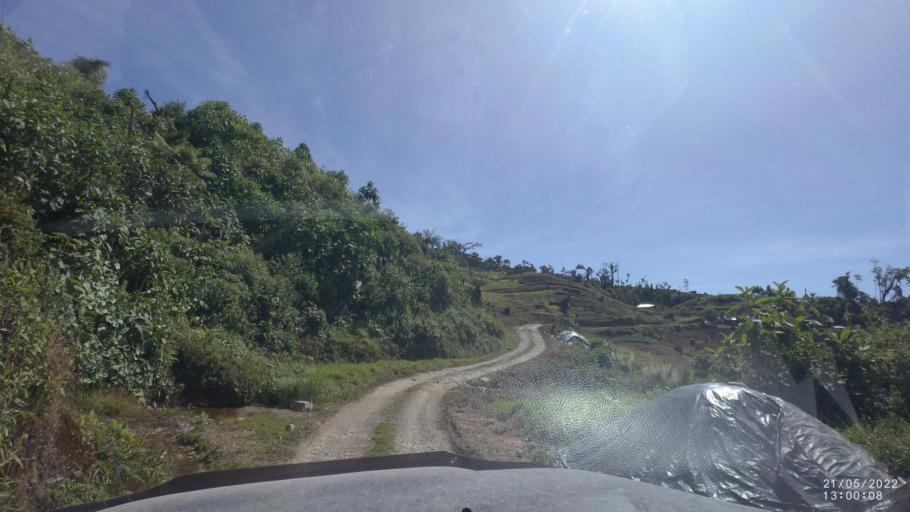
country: BO
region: Cochabamba
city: Colomi
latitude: -17.1643
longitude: -65.9504
